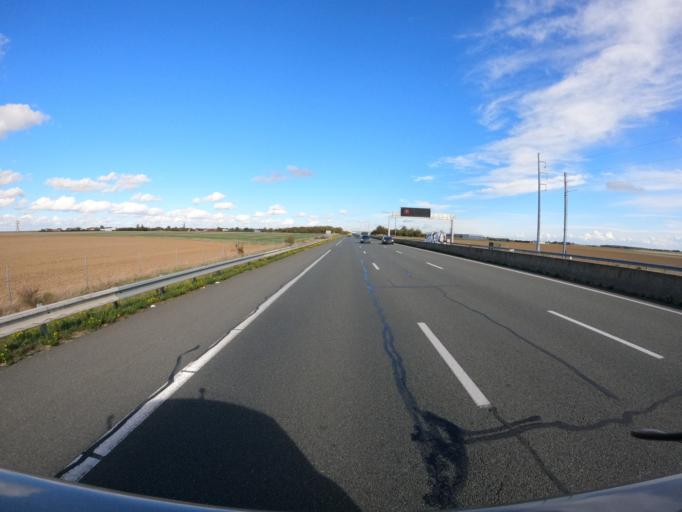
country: FR
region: Centre
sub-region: Departement d'Eure-et-Loir
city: Dammarie
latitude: 48.3507
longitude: 1.4220
